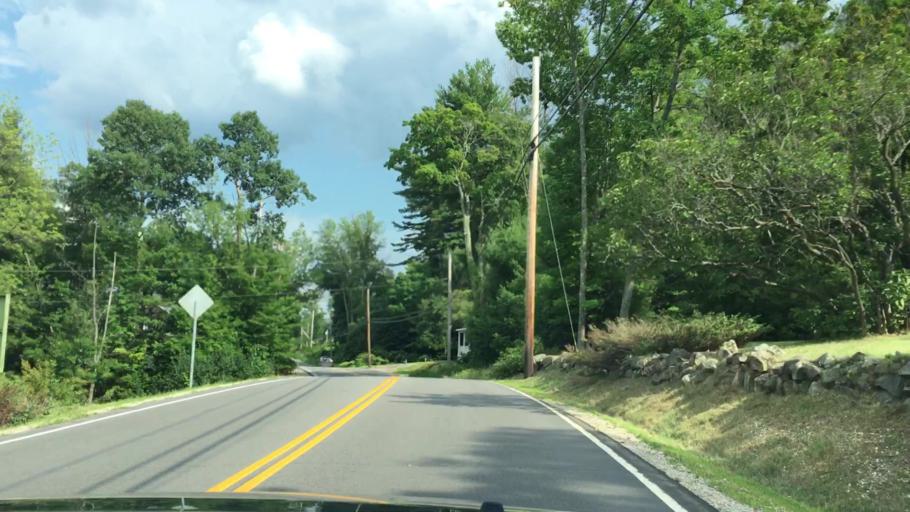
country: US
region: New Hampshire
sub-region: Belknap County
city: Gilford
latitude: 43.5620
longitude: -71.3344
